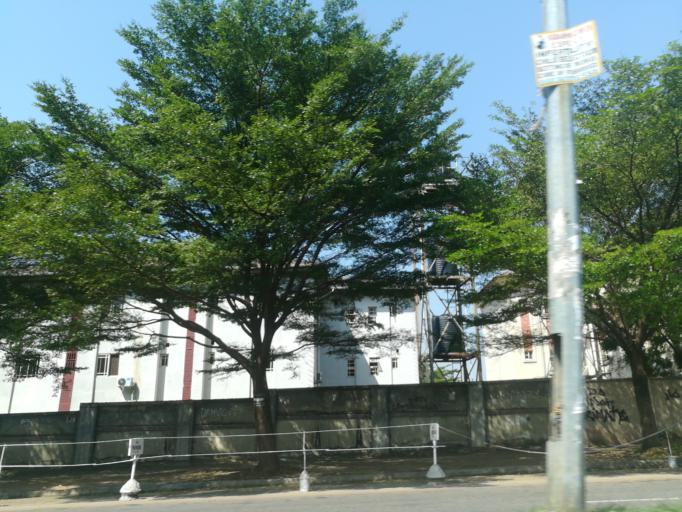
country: NG
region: Abuja Federal Capital Territory
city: Abuja
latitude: 9.0715
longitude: 7.4452
